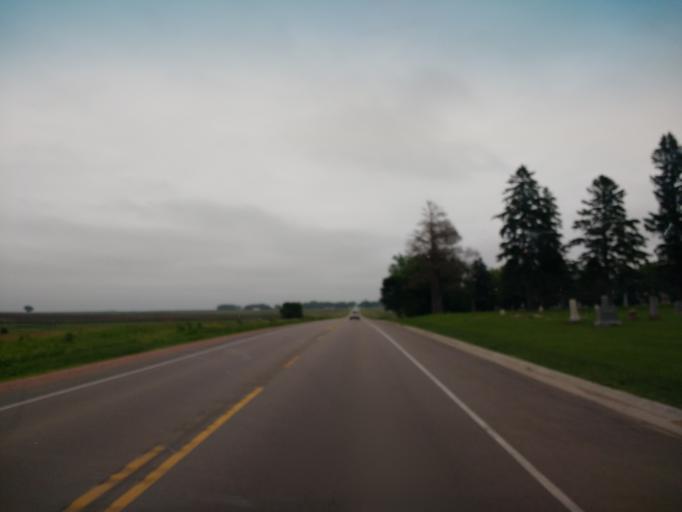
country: US
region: Iowa
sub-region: O'Brien County
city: Sanborn
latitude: 43.1861
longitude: -95.6821
